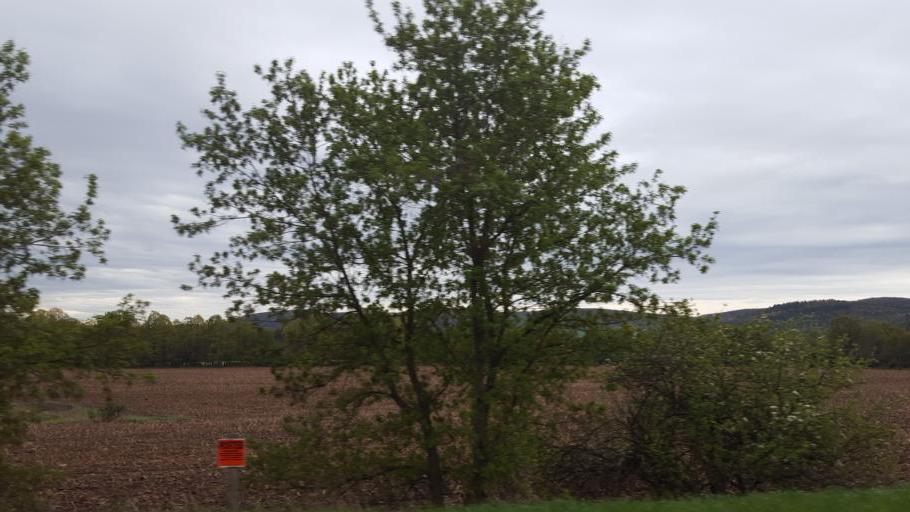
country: US
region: Pennsylvania
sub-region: Tioga County
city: Westfield
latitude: 42.0024
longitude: -77.4840
